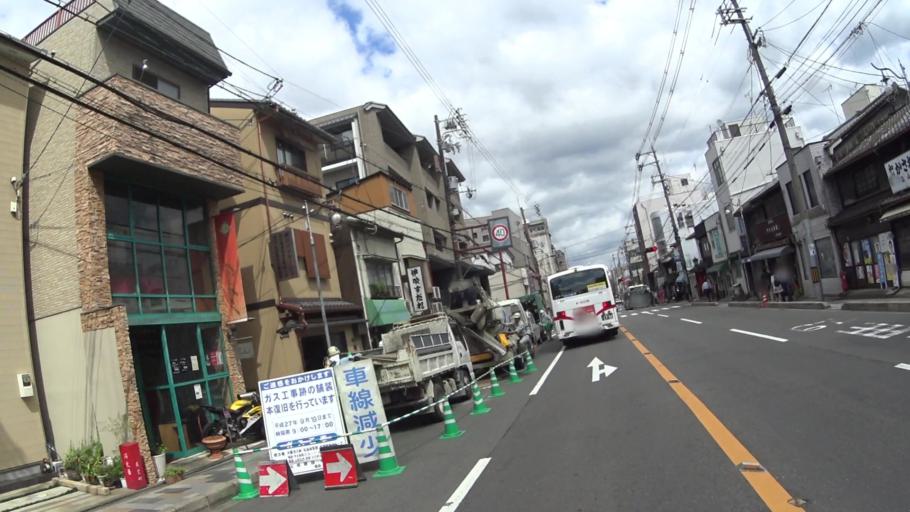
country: JP
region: Kyoto
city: Kyoto
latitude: 34.9973
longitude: 135.7769
